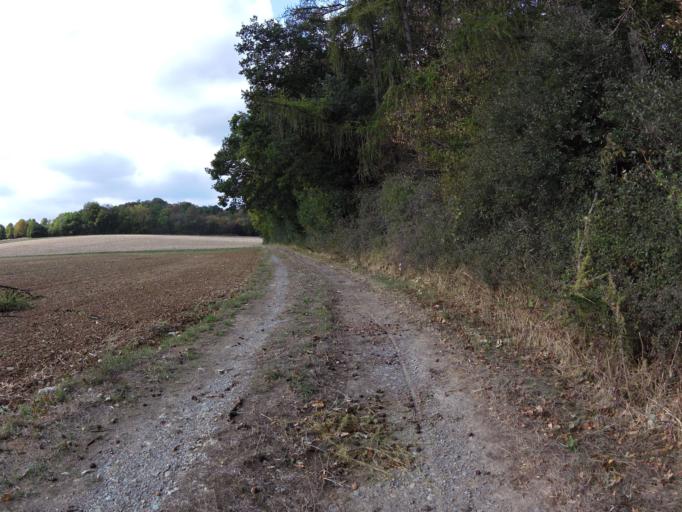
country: DE
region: Bavaria
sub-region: Regierungsbezirk Unterfranken
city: Reichenberg
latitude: 49.7362
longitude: 9.9389
